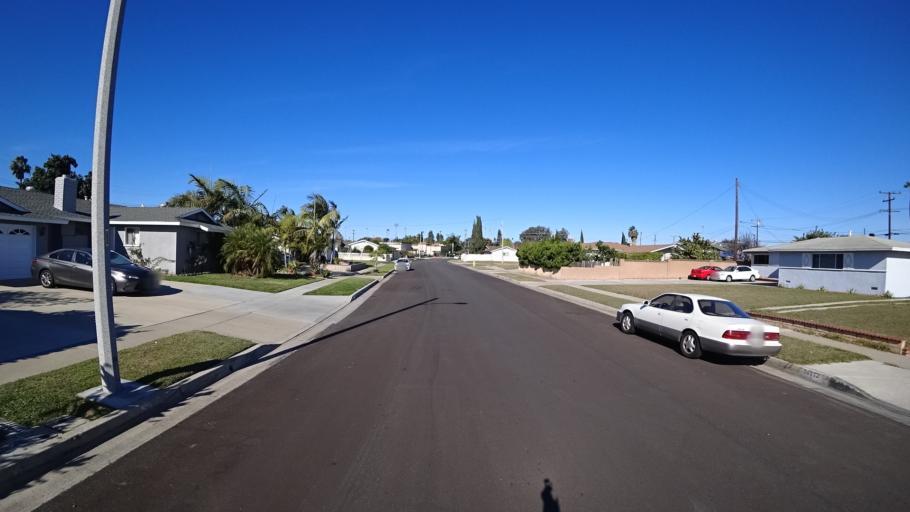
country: US
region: California
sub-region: Orange County
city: Midway City
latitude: 33.7578
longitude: -117.9653
